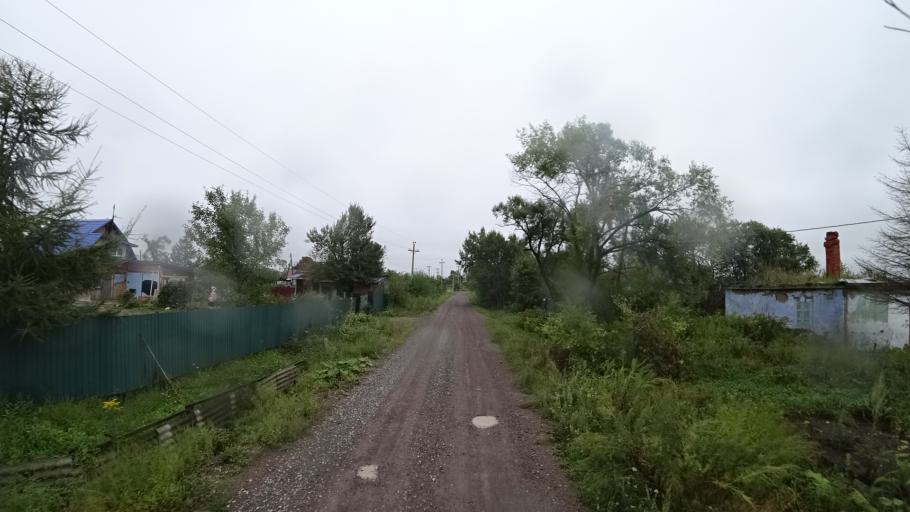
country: RU
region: Primorskiy
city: Monastyrishche
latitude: 44.1908
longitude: 132.4201
